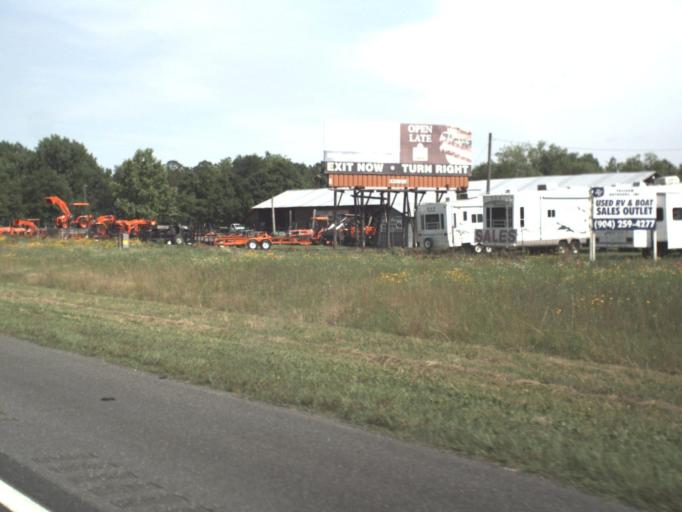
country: US
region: Florida
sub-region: Baker County
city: Macclenny
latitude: 30.2594
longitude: -82.1330
